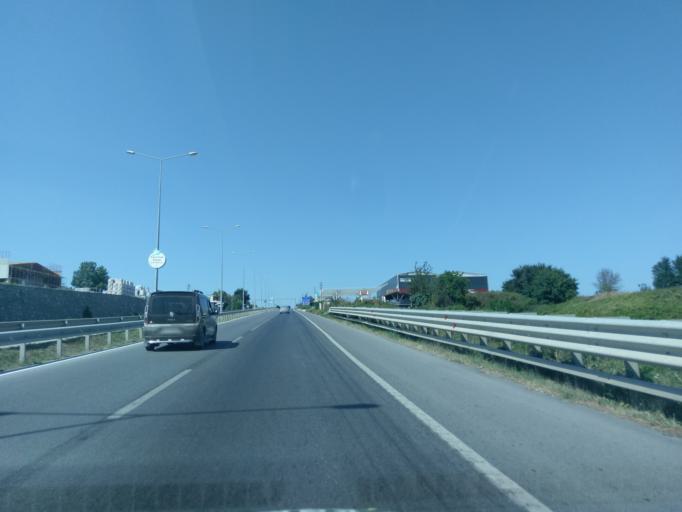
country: TR
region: Samsun
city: Bafra
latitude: 41.5435
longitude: 35.9304
